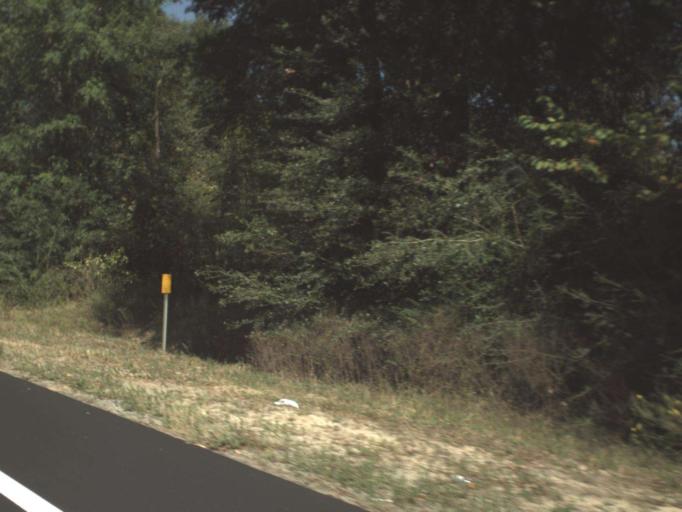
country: US
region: Florida
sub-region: Walton County
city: DeFuniak Springs
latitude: 30.7760
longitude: -86.1602
